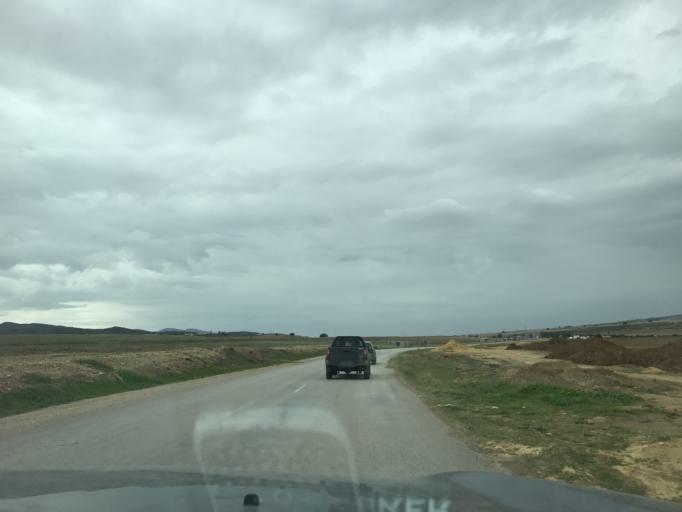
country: TN
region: Silyanah
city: Bu `Aradah
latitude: 36.2077
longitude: 9.7294
